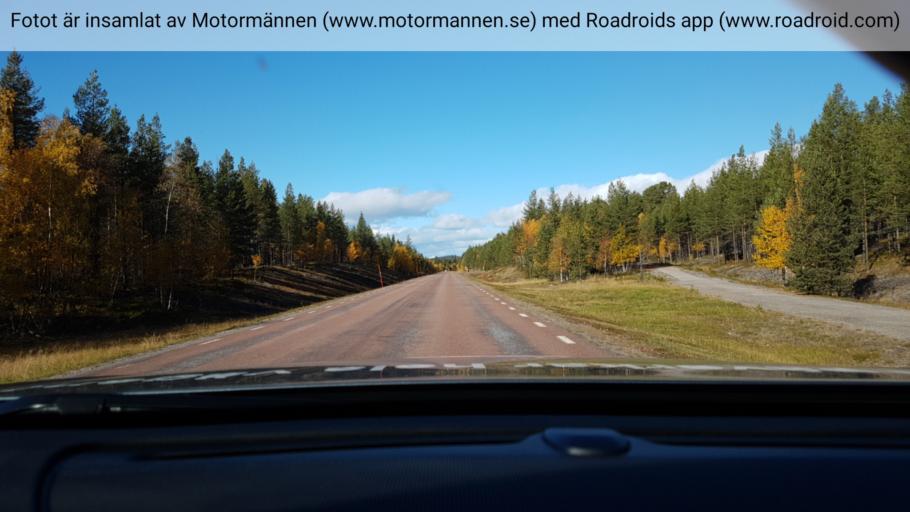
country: SE
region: Norrbotten
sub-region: Arjeplogs Kommun
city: Arjeplog
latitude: 66.0083
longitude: 18.1010
